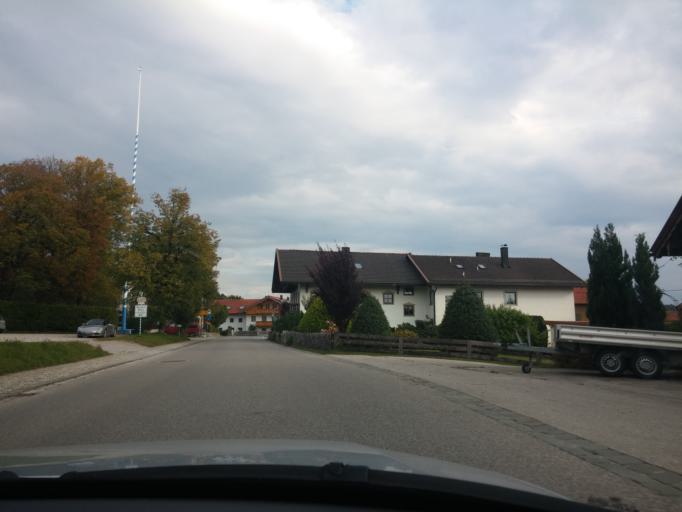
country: DE
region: Bavaria
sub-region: Upper Bavaria
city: Dietramszell
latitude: 47.8552
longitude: 11.5875
